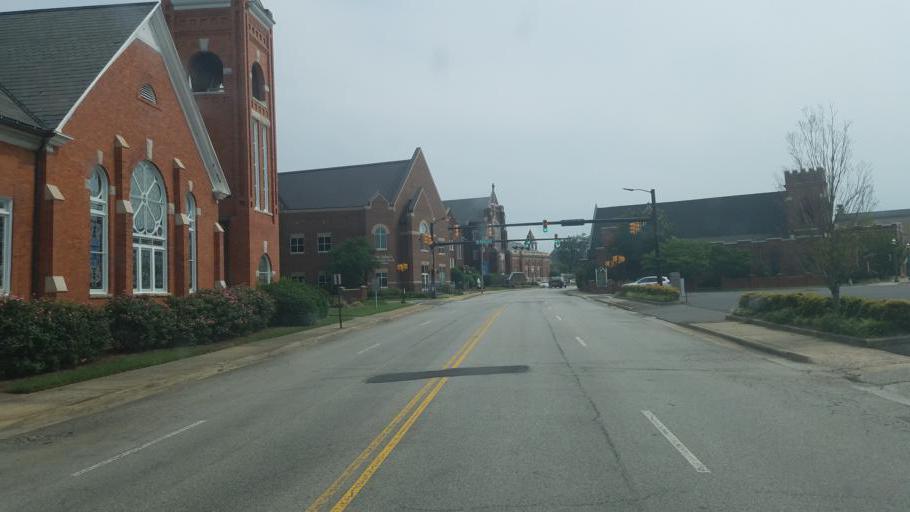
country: US
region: South Carolina
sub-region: York County
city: Rock Hill
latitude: 34.9269
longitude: -81.0241
